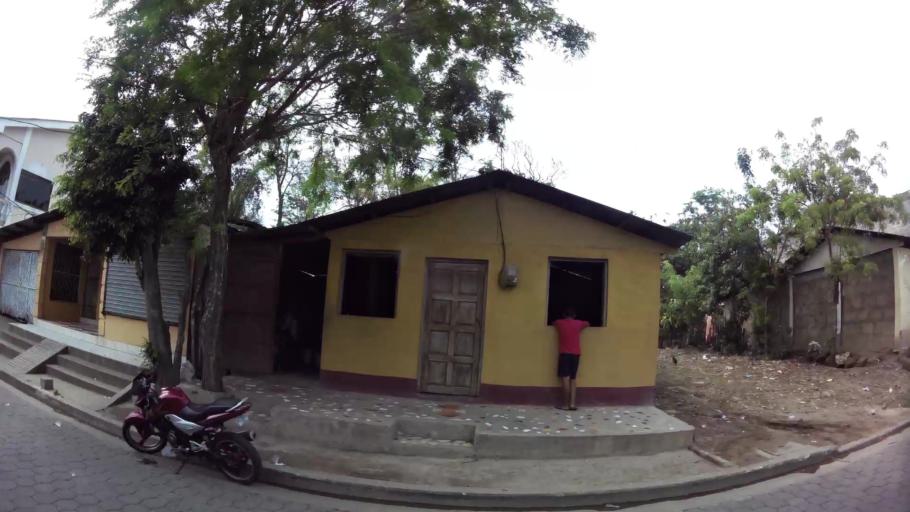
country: NI
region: Masaya
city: Catarina
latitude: 11.9116
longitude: -86.0764
